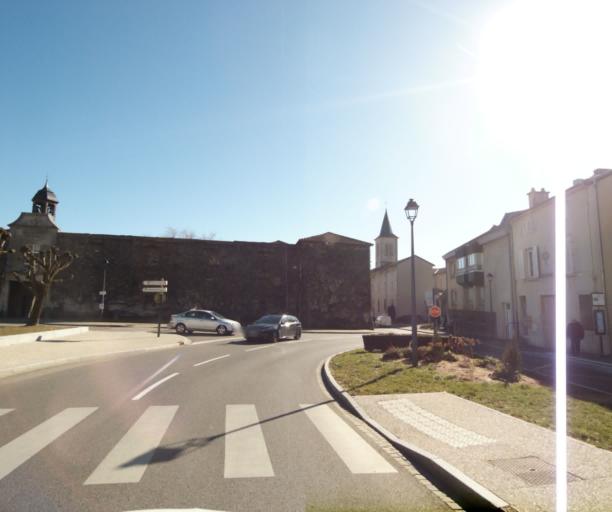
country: FR
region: Lorraine
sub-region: Departement de Meurthe-et-Moselle
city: Ludres
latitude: 48.6214
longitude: 6.1616
